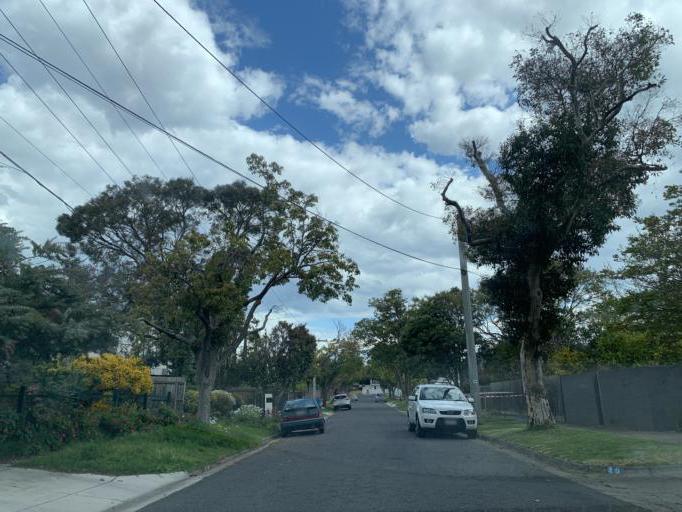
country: AU
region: Victoria
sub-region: Bayside
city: Hampton
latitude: -37.9329
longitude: 145.0158
